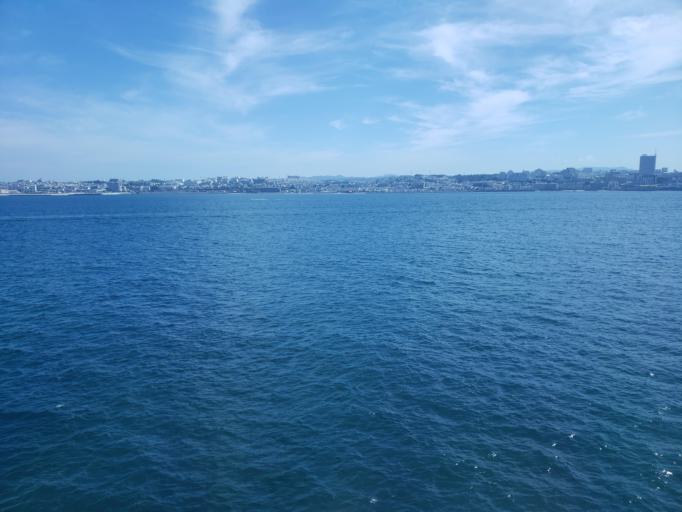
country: JP
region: Hyogo
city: Akashi
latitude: 34.6237
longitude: 135.0159
